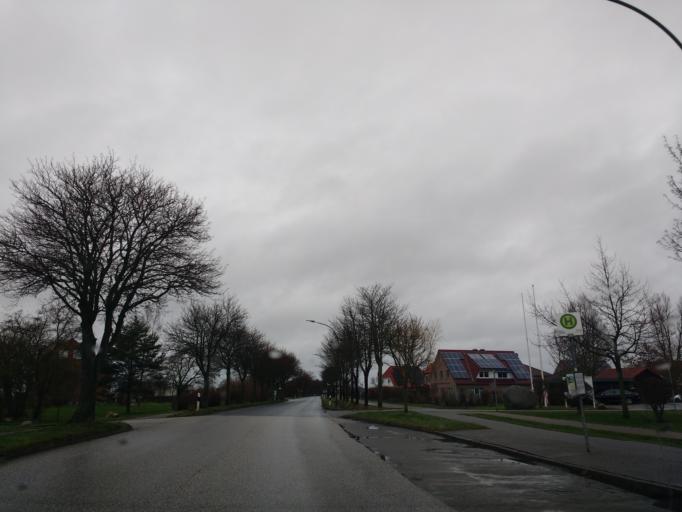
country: DE
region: Schleswig-Holstein
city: Fehmarn
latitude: 54.4444
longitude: 11.1991
